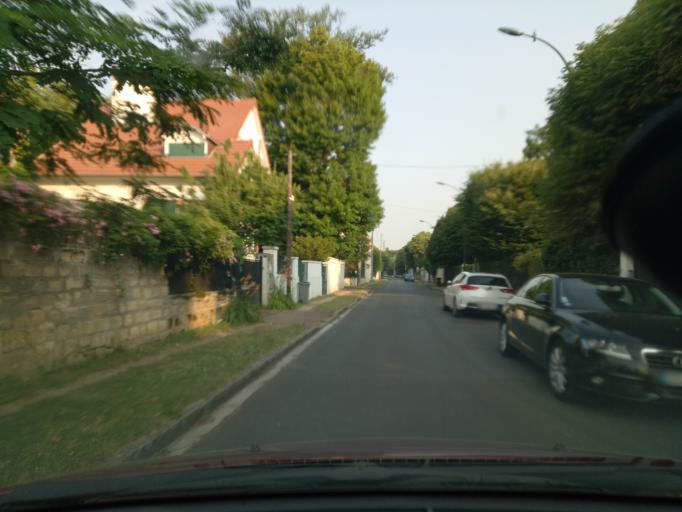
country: FR
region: Ile-de-France
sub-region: Departement des Yvelines
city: Croissy-sur-Seine
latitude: 48.8856
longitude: 2.1455
